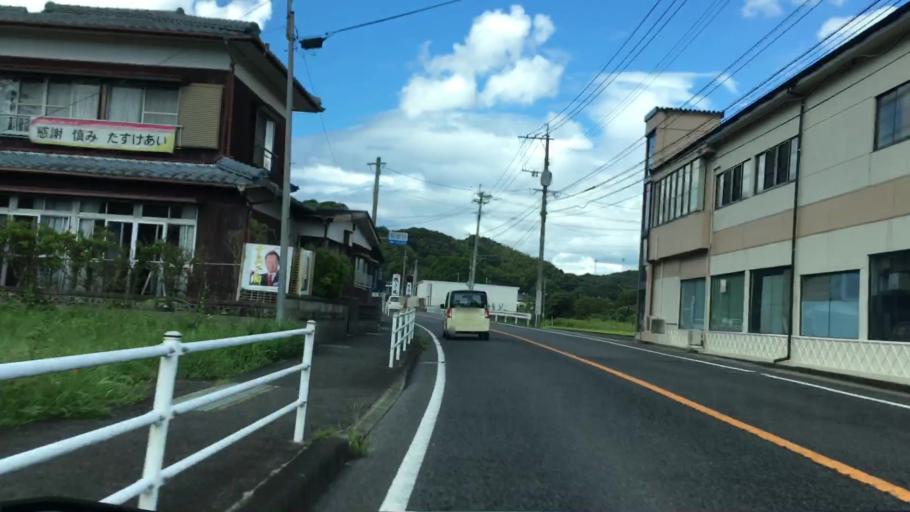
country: JP
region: Nagasaki
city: Sasebo
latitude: 33.1548
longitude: 129.8306
